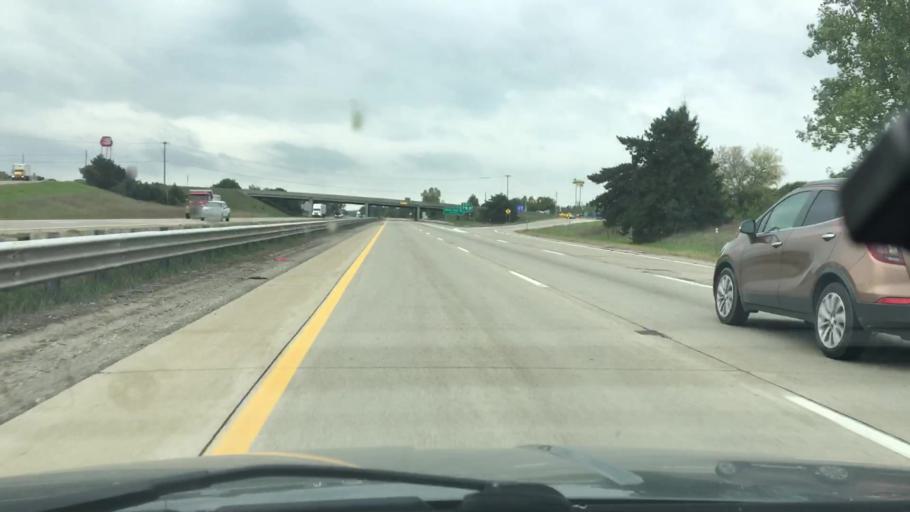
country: US
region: Michigan
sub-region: Genesee County
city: Fenton
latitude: 42.7922
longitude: -83.7370
